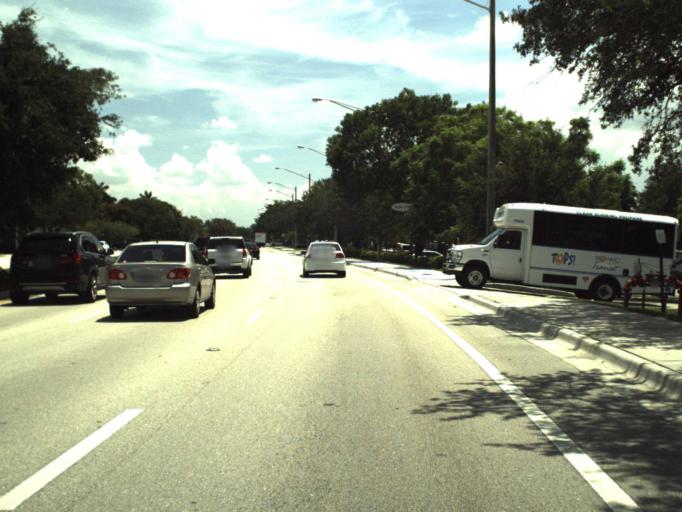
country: US
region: Florida
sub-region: Broward County
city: Coral Springs
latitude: 26.2523
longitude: -80.2534
